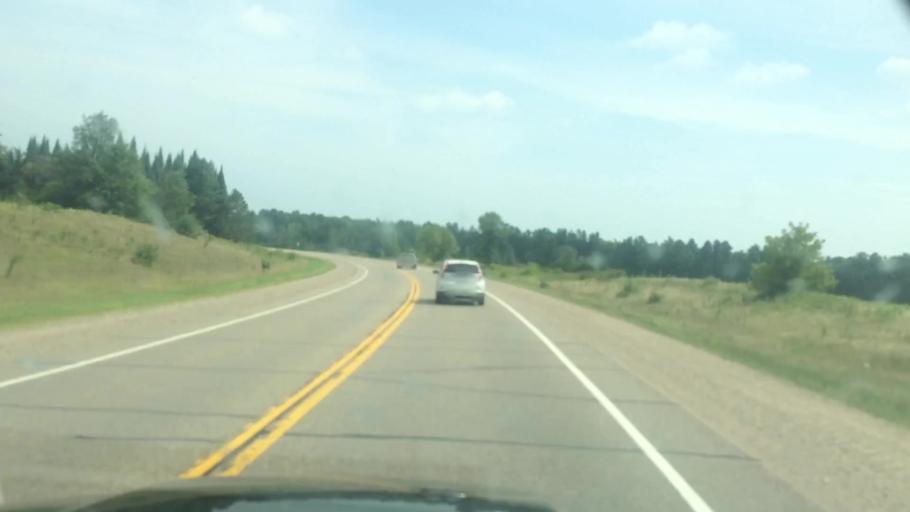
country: US
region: Wisconsin
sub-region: Langlade County
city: Antigo
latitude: 45.1622
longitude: -89.0158
